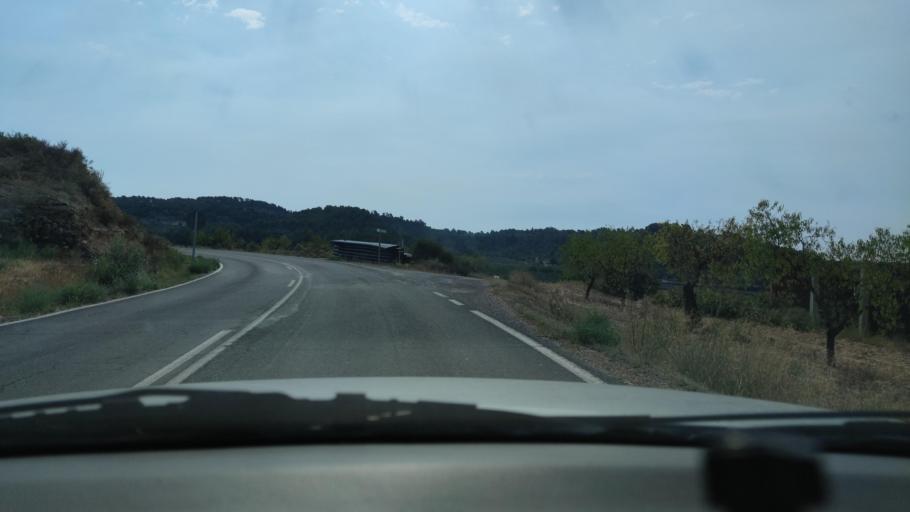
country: ES
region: Catalonia
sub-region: Provincia de Lleida
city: Arbeca
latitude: 41.5016
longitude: 0.9674
